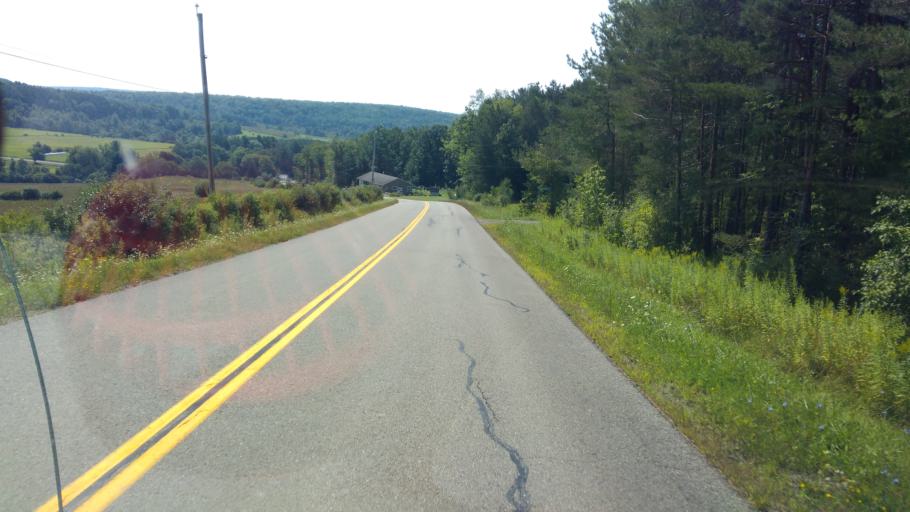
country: US
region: New York
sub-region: Allegany County
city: Belmont
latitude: 42.2782
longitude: -77.9934
